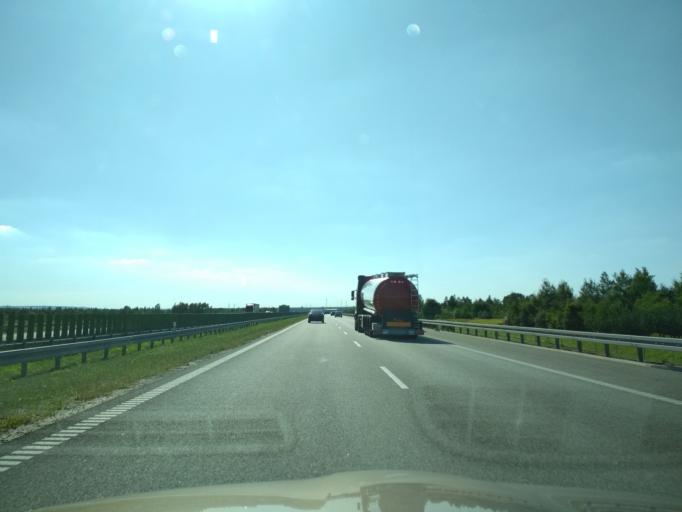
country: PL
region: Subcarpathian Voivodeship
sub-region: Powiat rzeszowski
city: Rudna Mala
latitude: 50.1067
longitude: 21.9578
